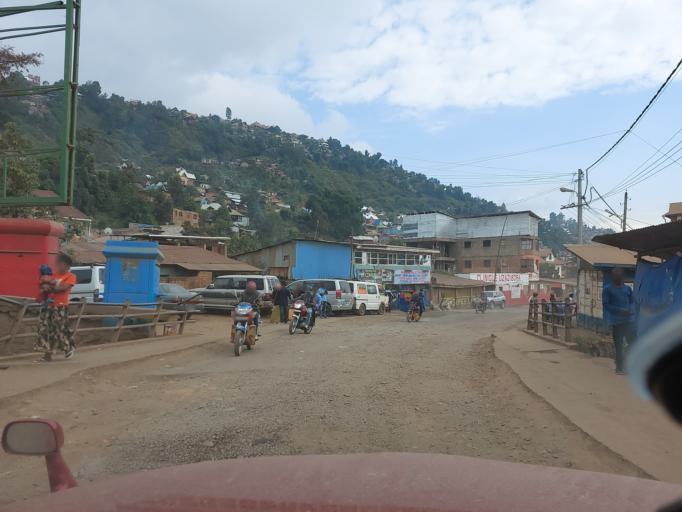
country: CD
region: South Kivu
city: Bukavu
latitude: -2.5149
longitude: 28.8490
